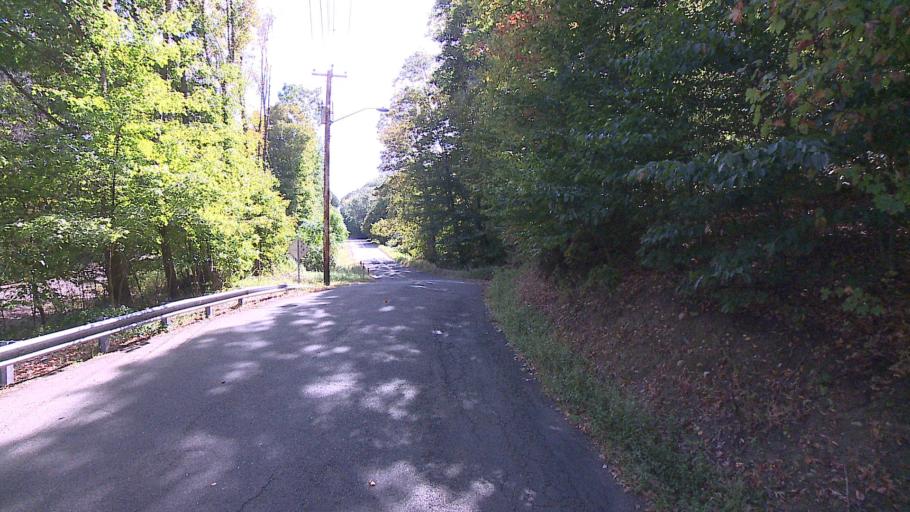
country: US
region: Connecticut
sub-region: Fairfield County
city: Shelton
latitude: 41.3481
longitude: -73.1309
